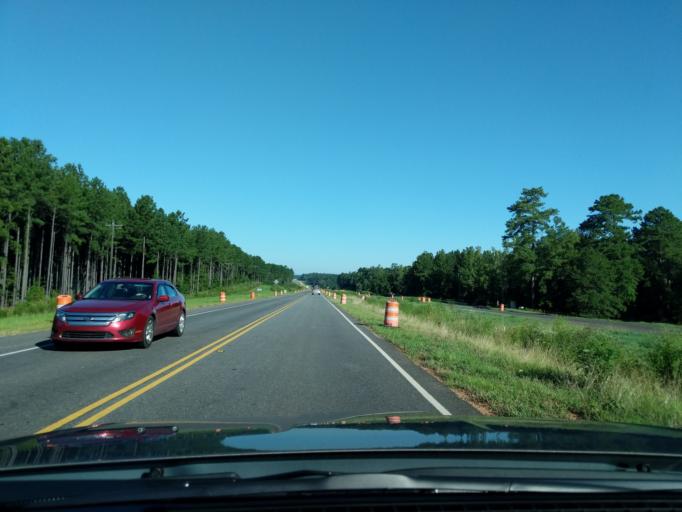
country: US
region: Georgia
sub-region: McDuffie County
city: Thomson
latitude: 33.5746
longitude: -82.5217
